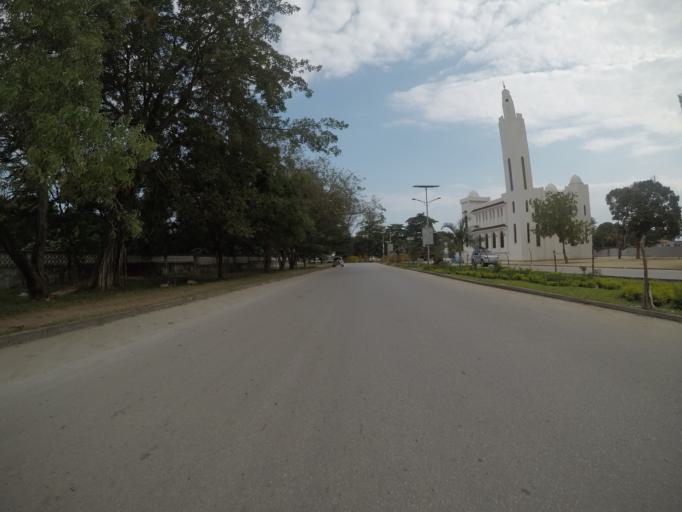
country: TZ
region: Zanzibar Urban/West
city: Zanzibar
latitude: -6.1731
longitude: 39.1988
